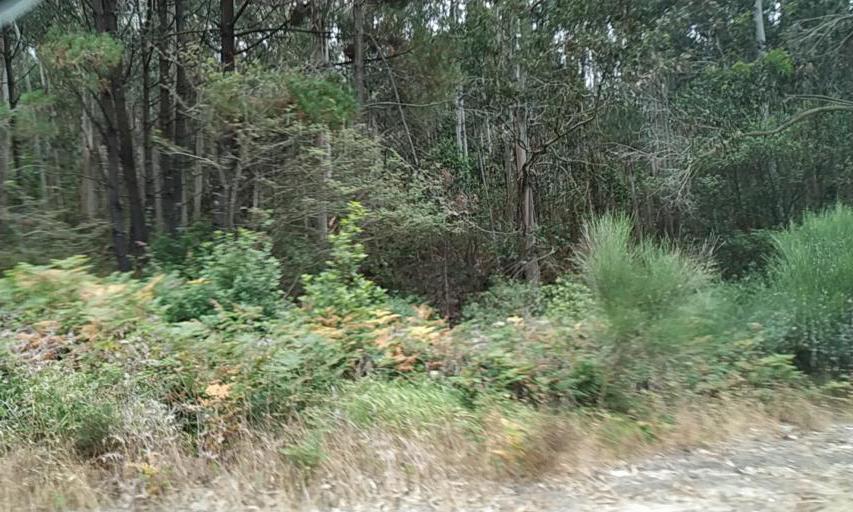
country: ES
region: Galicia
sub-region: Provincia de Pontevedra
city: Oia
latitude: 41.9607
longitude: -8.8836
